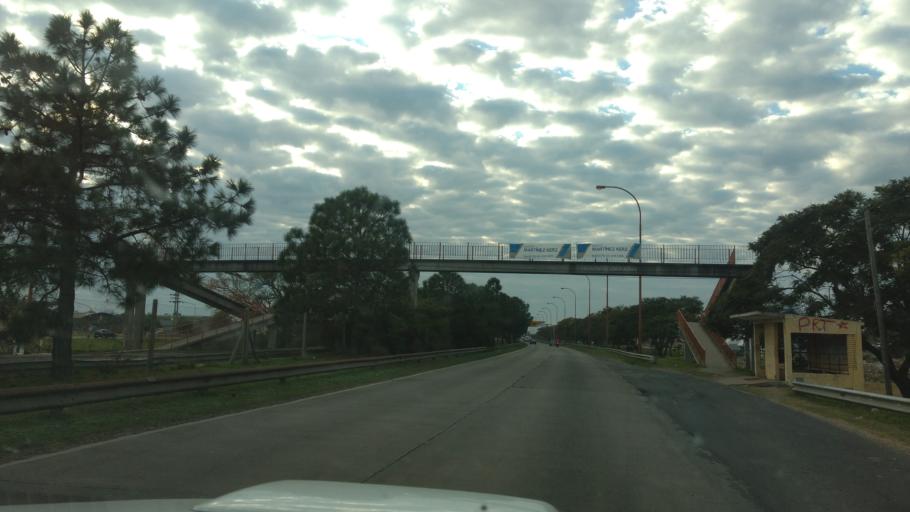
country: AR
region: Santa Fe
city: Santa Fe de la Vera Cruz
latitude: -31.6414
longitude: -60.6781
